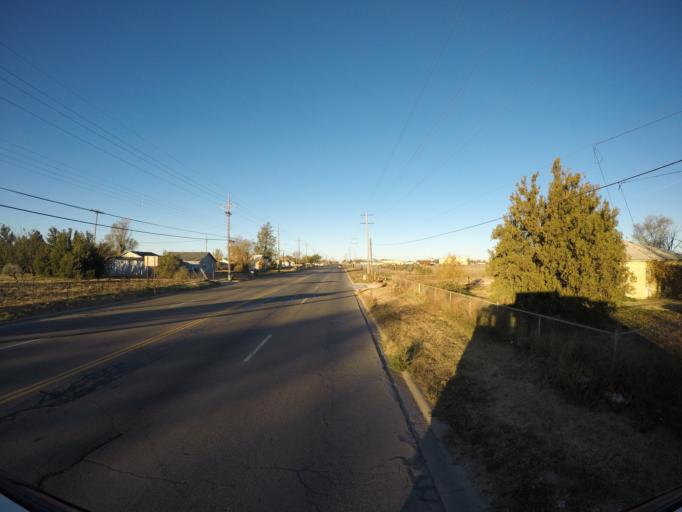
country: US
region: New Mexico
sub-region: Curry County
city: Clovis
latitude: 34.3903
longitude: -103.1873
